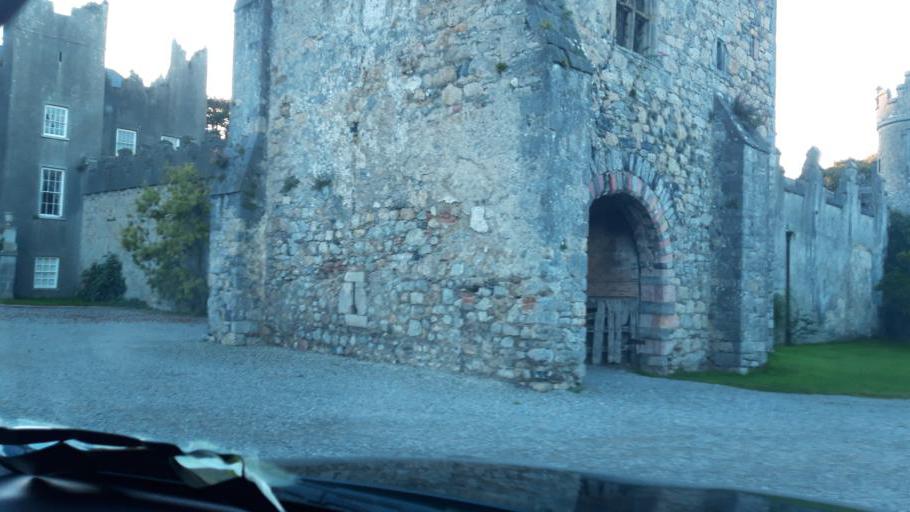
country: IE
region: Leinster
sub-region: Fingal County
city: Howth
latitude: 53.3863
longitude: -6.0787
